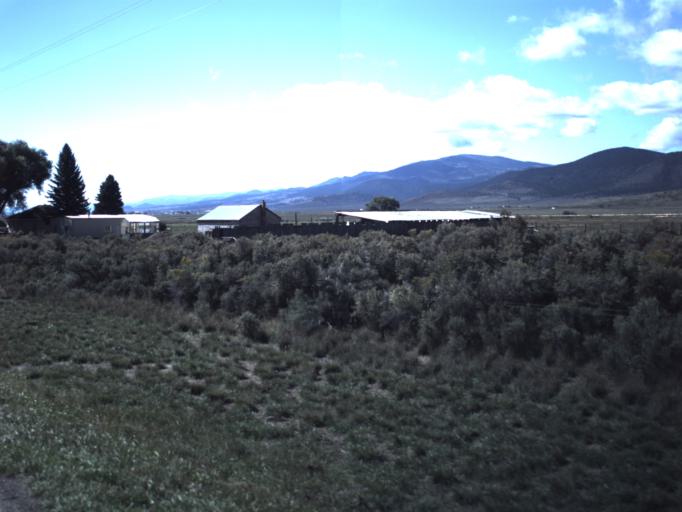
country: US
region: Utah
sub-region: Wayne County
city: Loa
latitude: 38.5010
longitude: -111.8814
